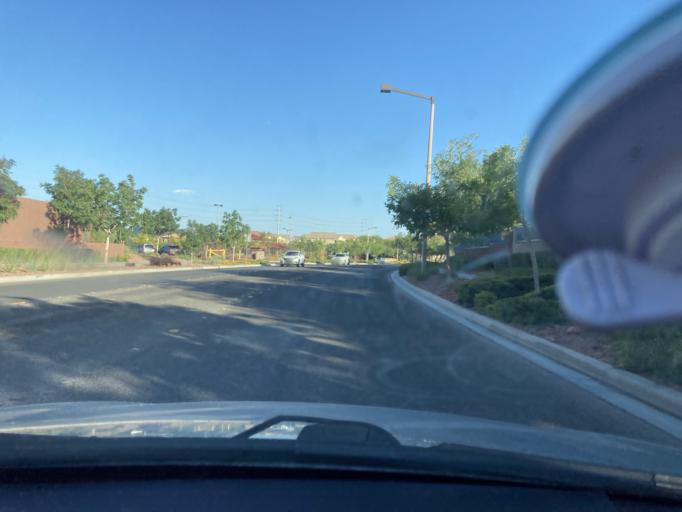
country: US
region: Nevada
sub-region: Clark County
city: Summerlin South
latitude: 36.1552
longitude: -115.3411
